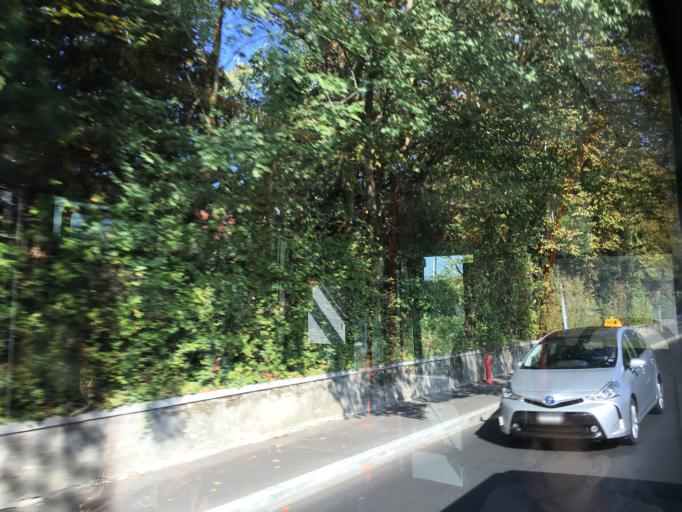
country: CH
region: Geneva
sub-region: Geneva
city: Geneve
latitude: 46.2147
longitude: 6.1414
